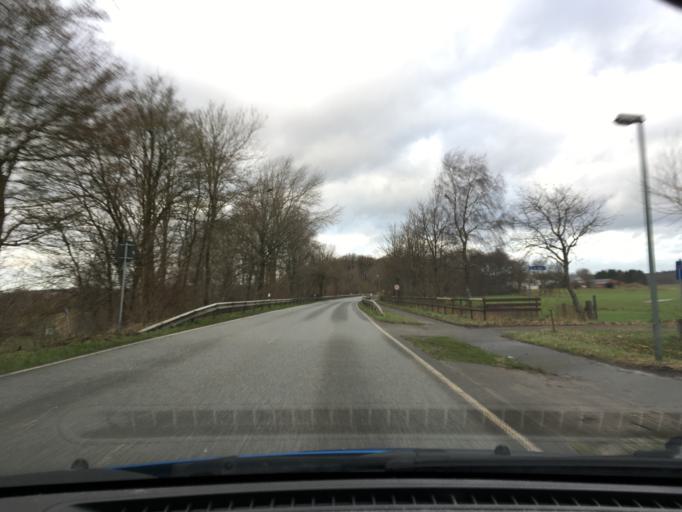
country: DE
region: Schleswig-Holstein
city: Kaaks
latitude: 53.9929
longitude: 9.4903
